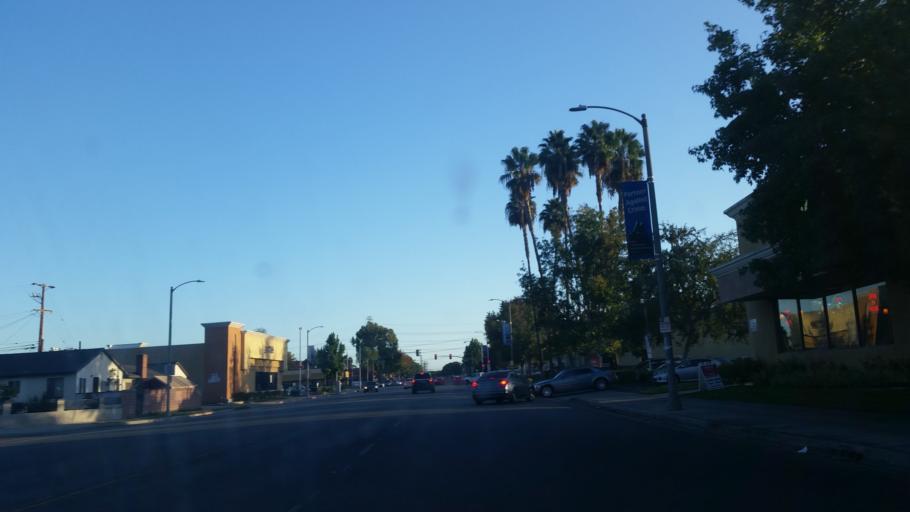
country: US
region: California
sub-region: Los Angeles County
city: Lakewood
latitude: 33.8600
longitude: -118.1172
